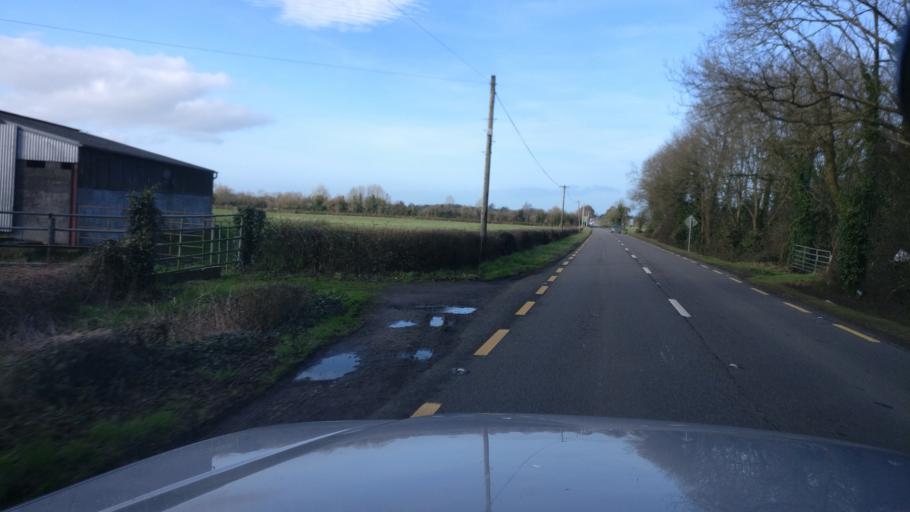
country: IE
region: Leinster
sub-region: Laois
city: Mountmellick
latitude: 53.0853
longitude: -7.3331
